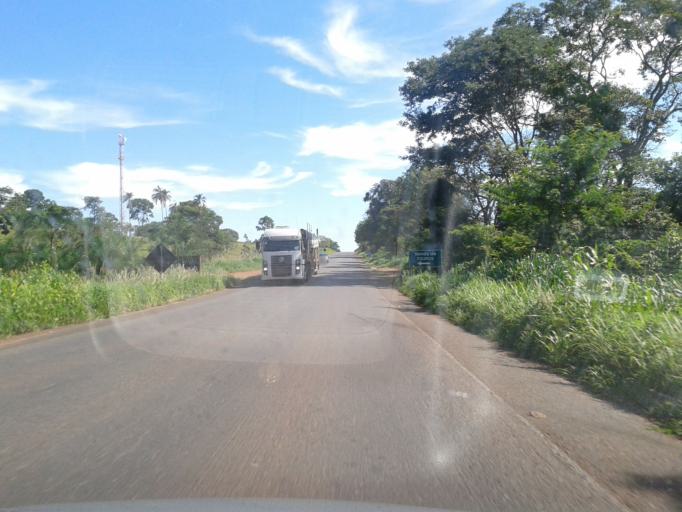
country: BR
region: Goias
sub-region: Piracanjuba
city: Piracanjuba
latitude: -17.2213
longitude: -48.7118
